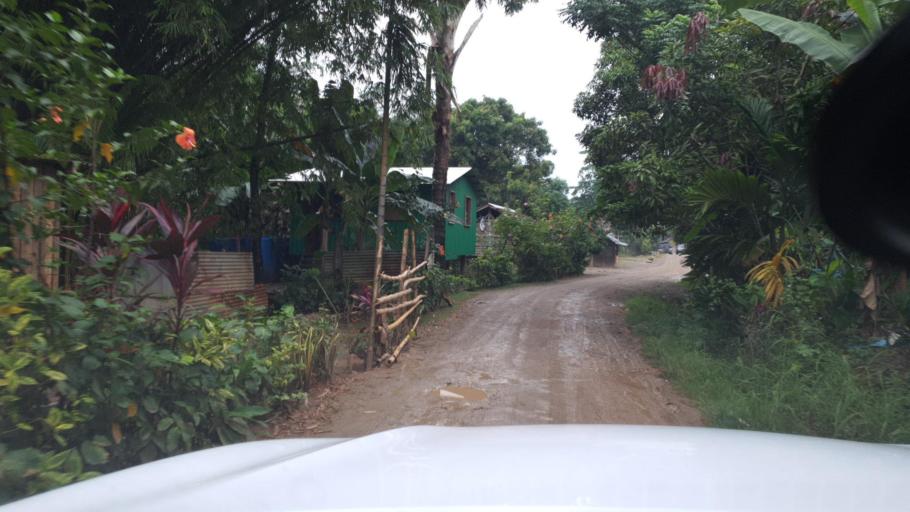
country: SB
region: Guadalcanal
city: Honiara
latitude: -9.4452
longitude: 159.9784
